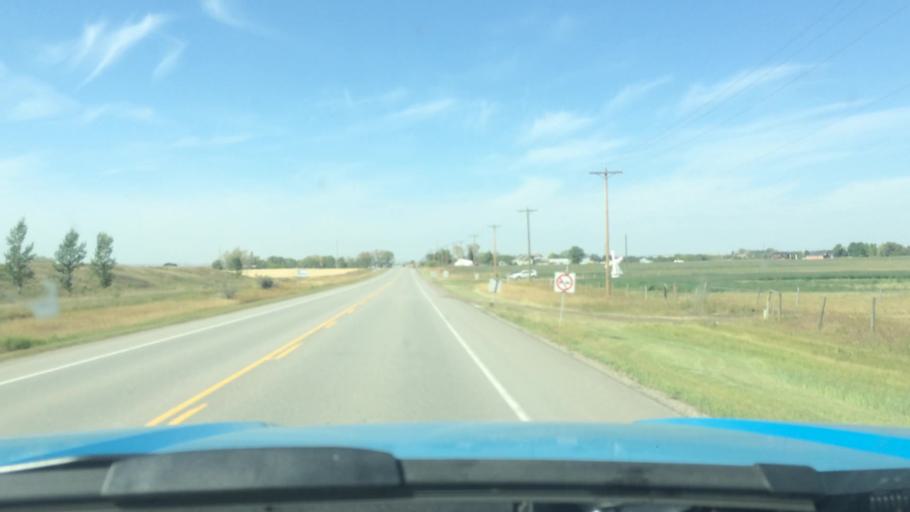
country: CA
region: Alberta
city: Airdrie
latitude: 51.2128
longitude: -113.9492
